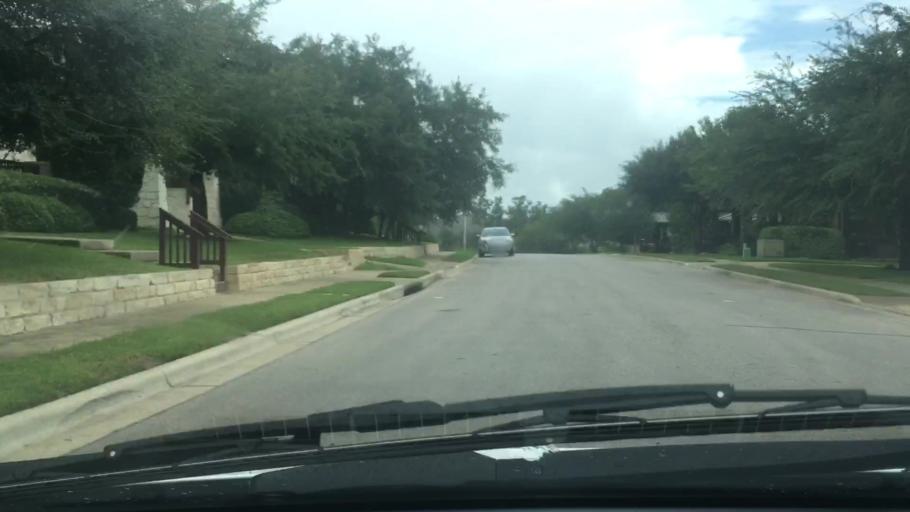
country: US
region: Texas
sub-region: Williamson County
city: Anderson Mill
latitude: 30.4533
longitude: -97.8567
